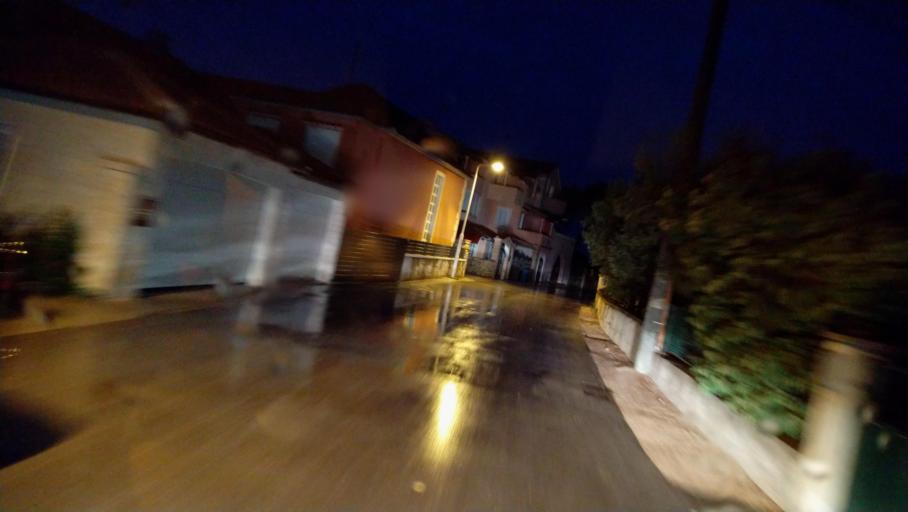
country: HR
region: Sibensko-Kniniska
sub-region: Grad Sibenik
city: Brodarica
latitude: 43.6787
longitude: 15.9184
